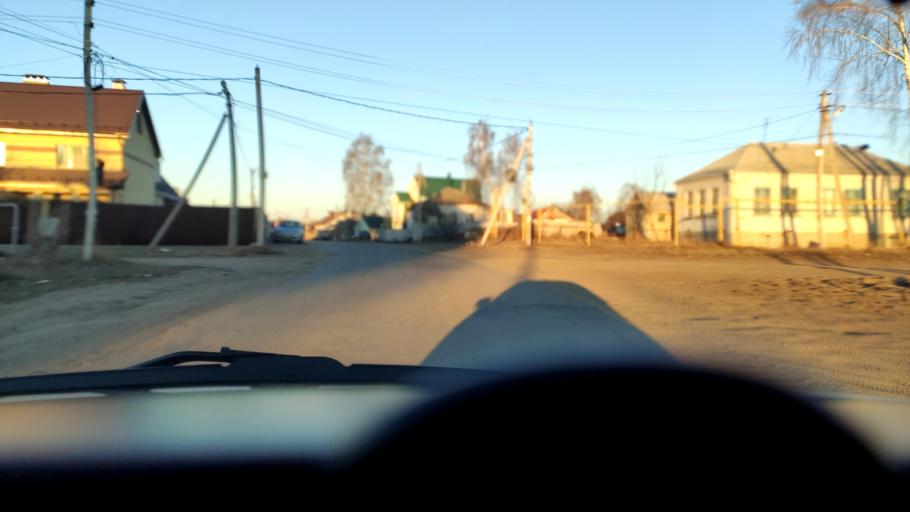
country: RU
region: Voronezj
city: Podgornoye
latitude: 51.7390
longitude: 39.1543
